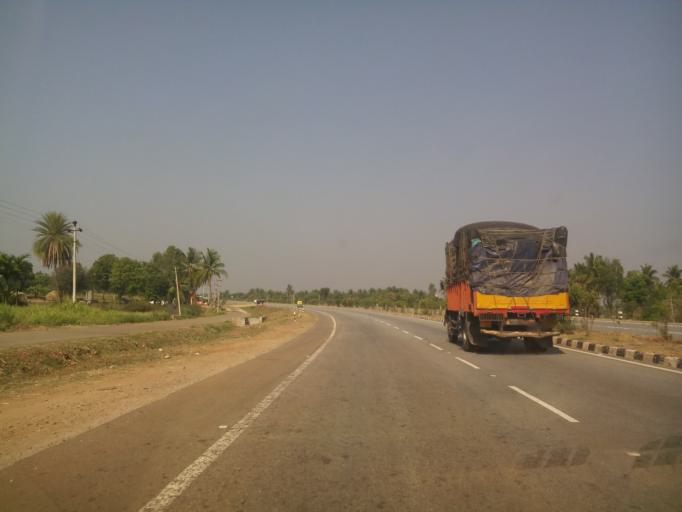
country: IN
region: Karnataka
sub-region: Tumkur
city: Kunigal
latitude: 13.0053
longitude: 76.9797
